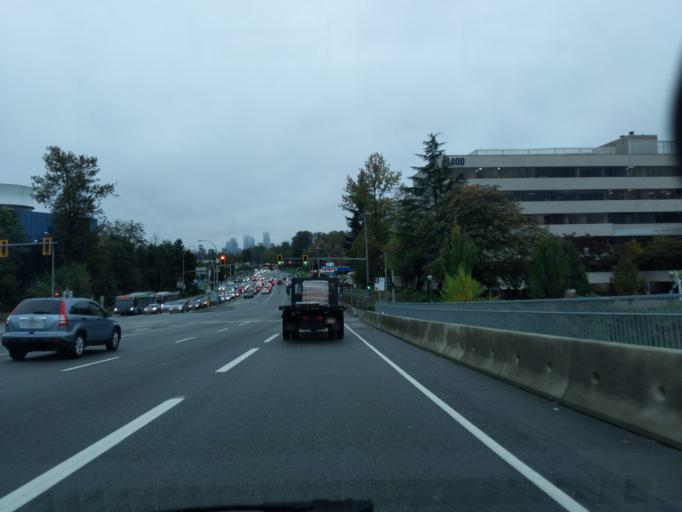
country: CA
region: British Columbia
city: Burnaby
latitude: 49.2567
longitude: -123.0044
